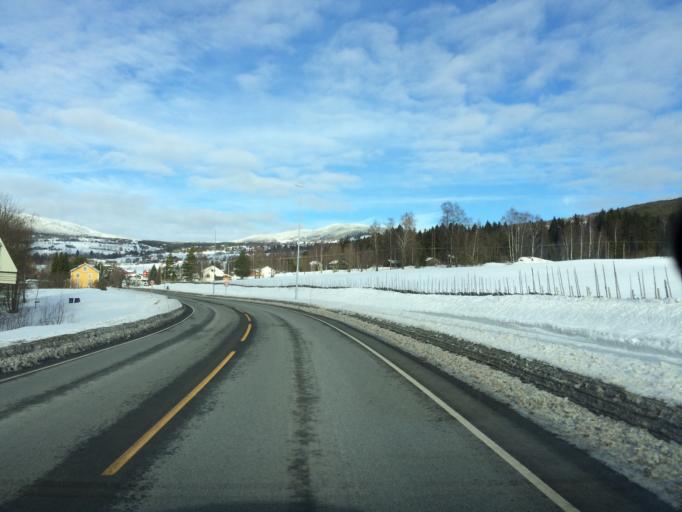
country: NO
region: Oppland
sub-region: Gausdal
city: Segalstad bru
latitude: 61.2092
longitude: 10.2977
